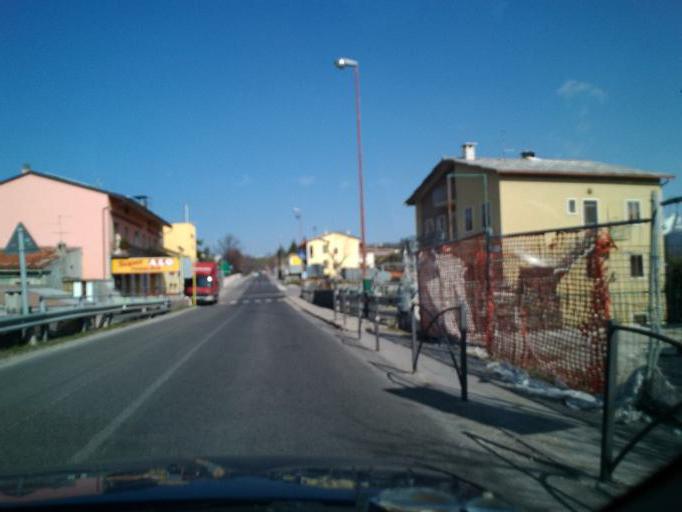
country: IT
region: Veneto
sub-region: Provincia di Verona
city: Cerro Veronese
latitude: 45.5790
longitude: 11.0432
